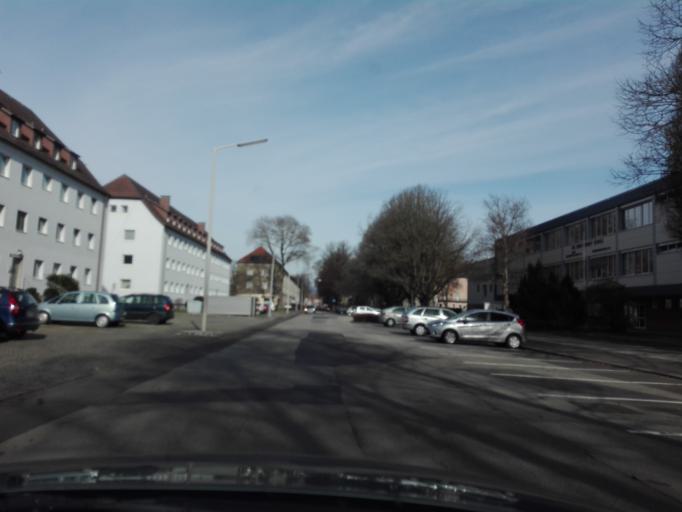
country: AT
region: Upper Austria
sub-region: Linz Stadt
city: Linz
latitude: 48.2716
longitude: 14.2883
